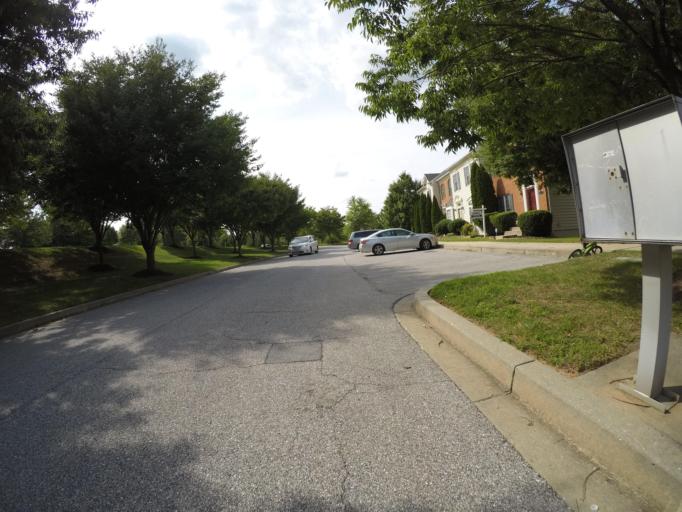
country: US
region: Maryland
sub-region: Howard County
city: Columbia
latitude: 39.3087
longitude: -76.8823
